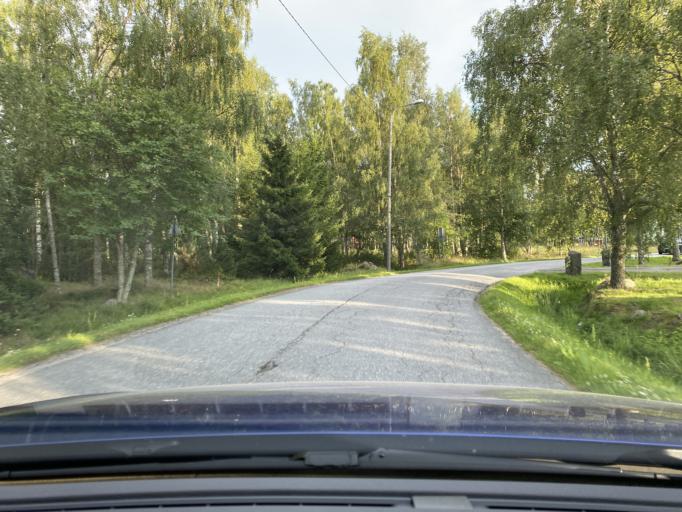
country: FI
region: Ostrobothnia
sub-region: Vaasa
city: Korsnaes
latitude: 62.9683
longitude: 21.1930
